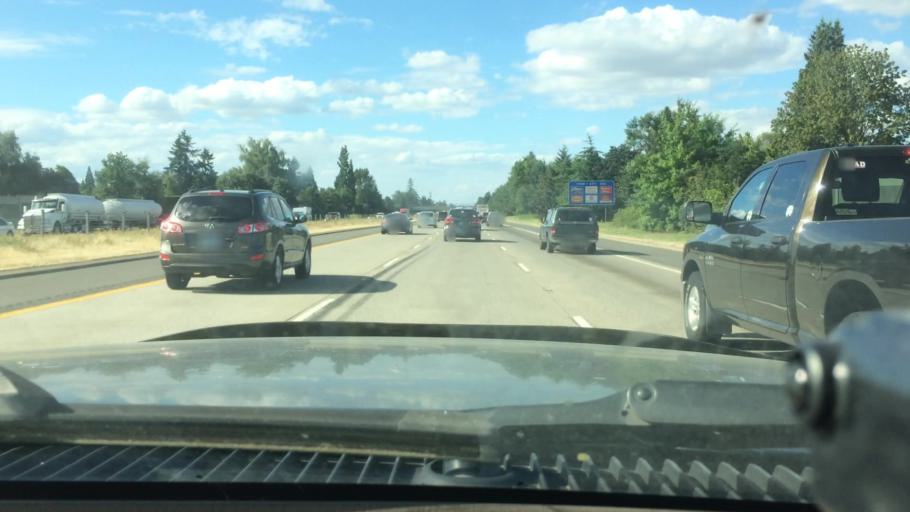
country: US
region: Oregon
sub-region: Marion County
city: Four Corners
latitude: 44.9336
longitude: -122.9902
